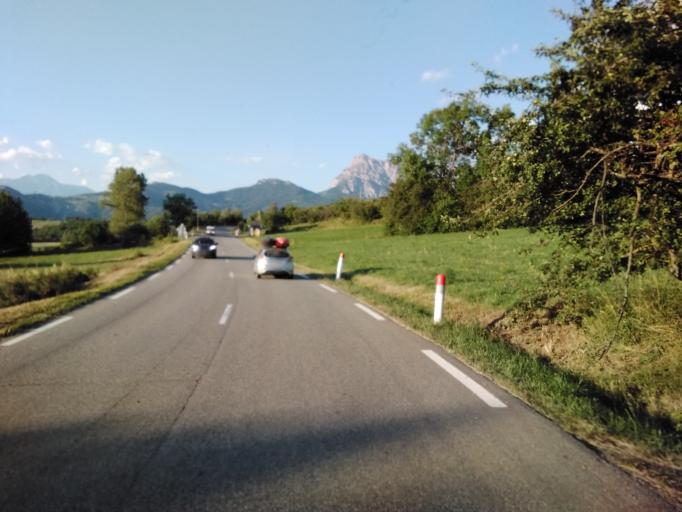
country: FR
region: Provence-Alpes-Cote d'Azur
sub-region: Departement des Alpes-de-Haute-Provence
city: Seyne-les-Alpes
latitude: 44.4459
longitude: 6.3299
